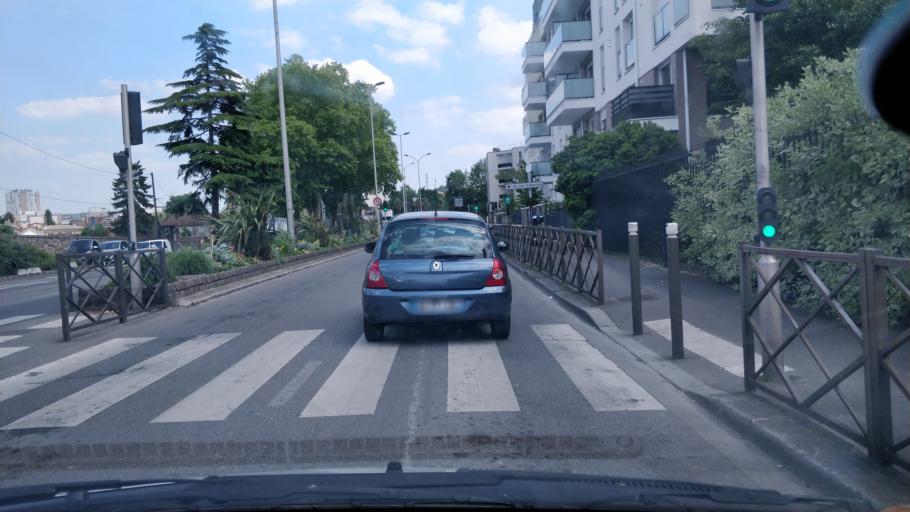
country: FR
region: Ile-de-France
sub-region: Departement de Seine-Saint-Denis
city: Rosny-sous-Bois
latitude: 48.8775
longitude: 2.4831
